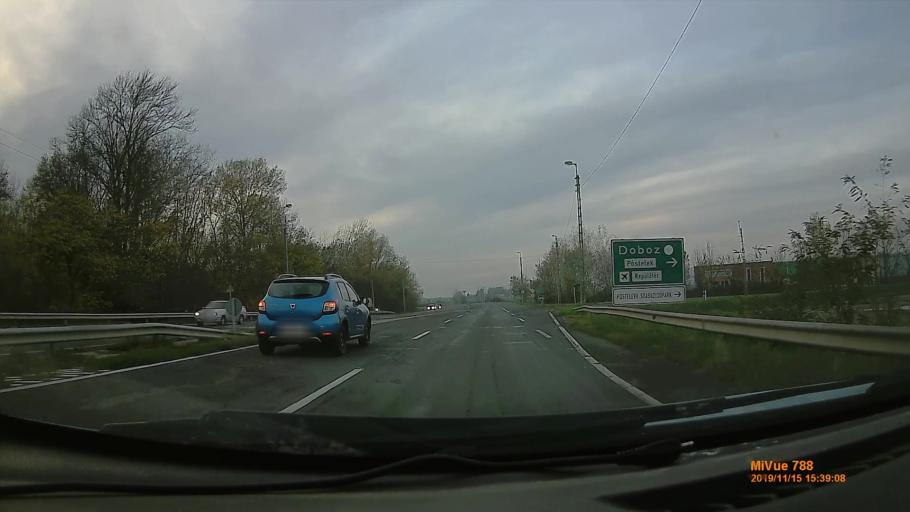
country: HU
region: Bekes
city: Bekescsaba
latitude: 46.6723
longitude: 21.1750
